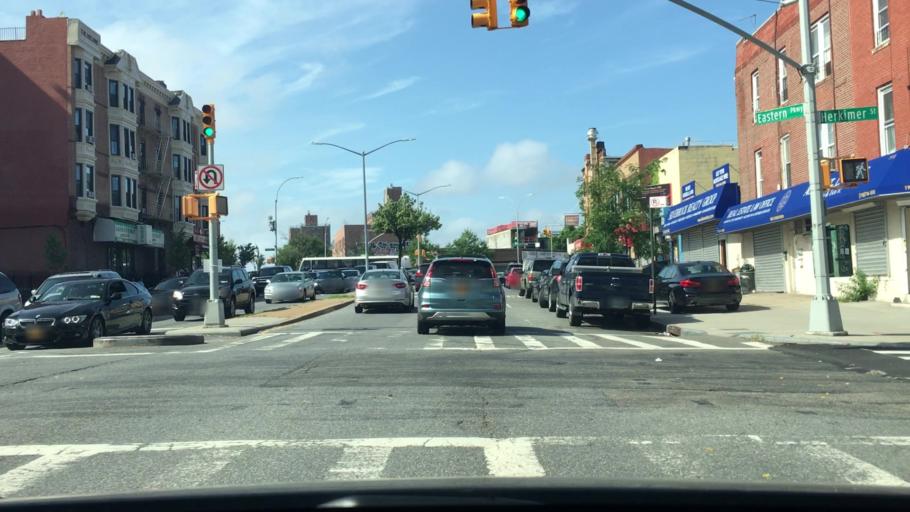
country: US
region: New York
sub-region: Kings County
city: East New York
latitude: 40.6773
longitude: -73.9079
